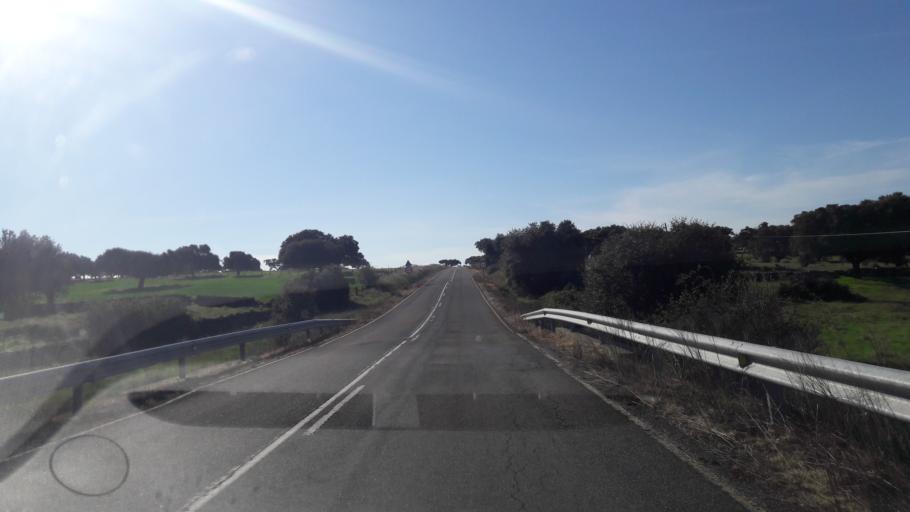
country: ES
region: Castille and Leon
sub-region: Provincia de Salamanca
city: Puente del Congosto
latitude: 40.5353
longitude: -5.5294
